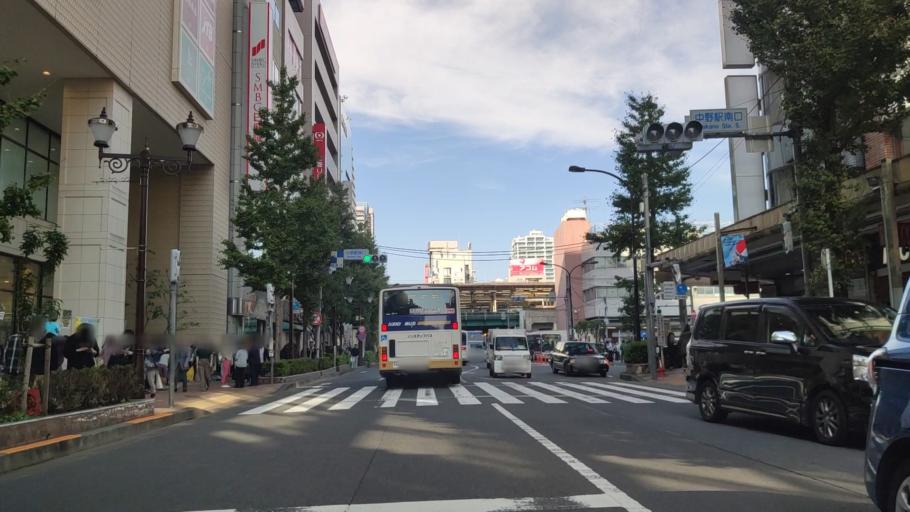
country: JP
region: Tokyo
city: Tokyo
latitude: 35.7045
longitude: 139.6654
